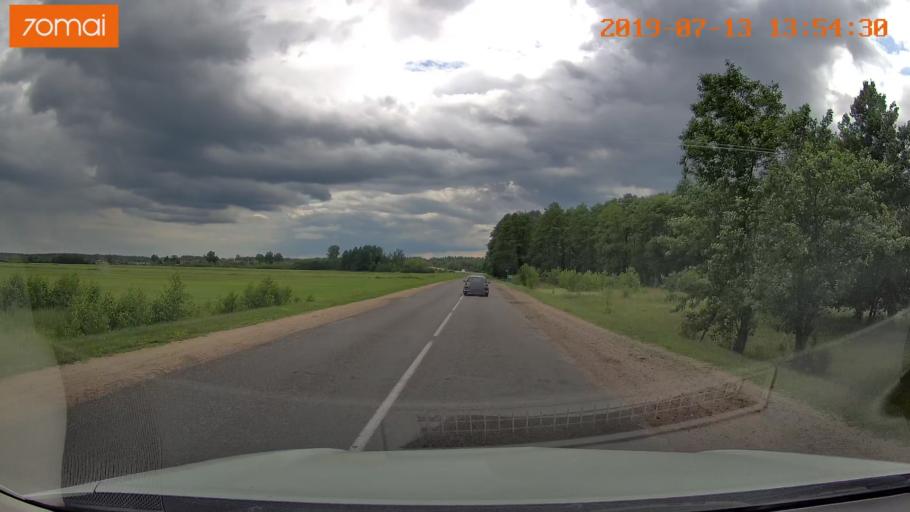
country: BY
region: Mogilev
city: Asipovichy
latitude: 53.2849
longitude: 28.6565
